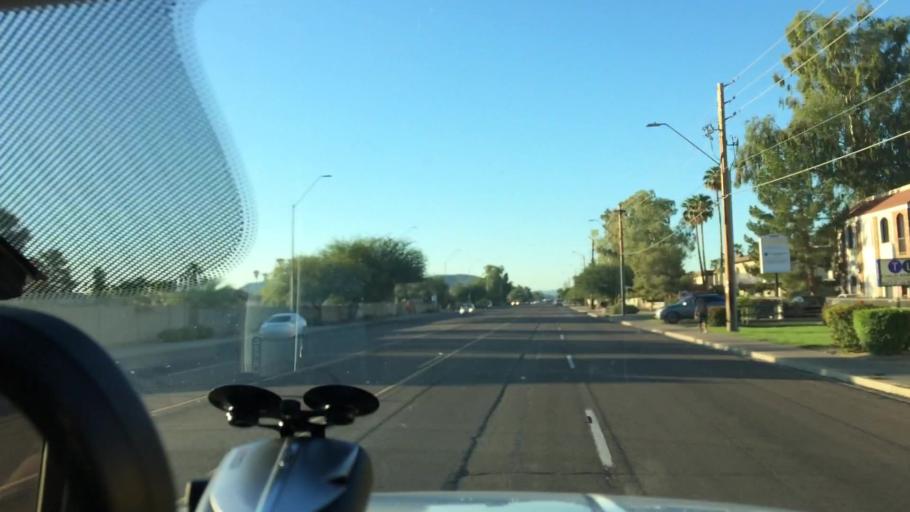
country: US
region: Arizona
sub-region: Maricopa County
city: Glendale
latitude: 33.6527
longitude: -112.0998
